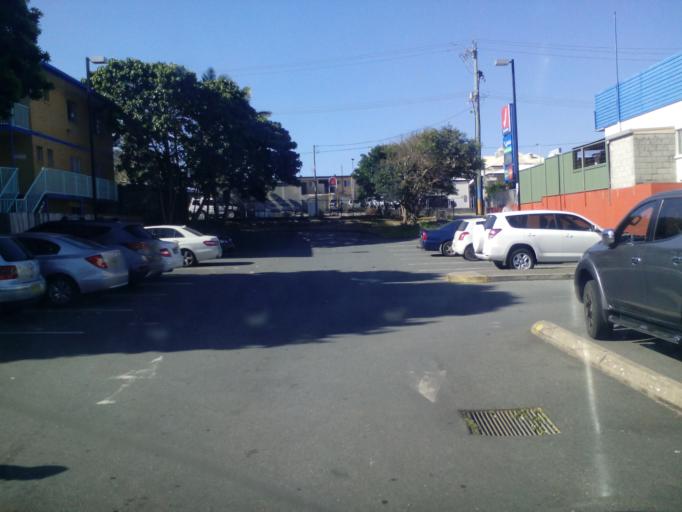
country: AU
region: New South Wales
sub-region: Tweed
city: Kingscliff
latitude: -28.2559
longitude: 153.5750
